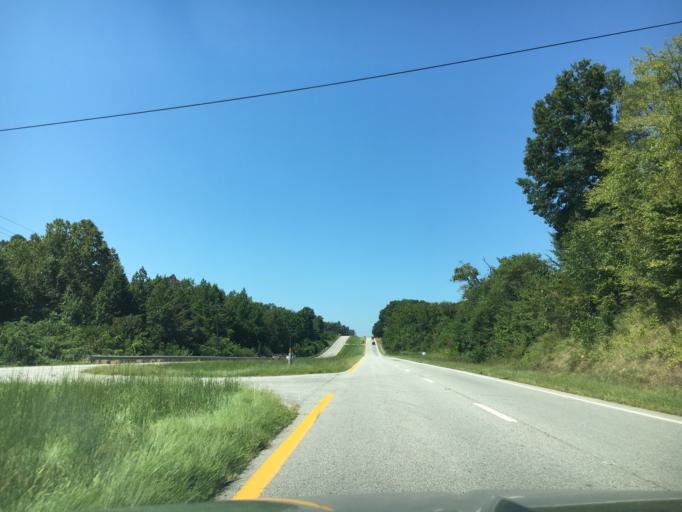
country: US
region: Virginia
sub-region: City of Danville
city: Danville
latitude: 36.5809
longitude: -79.2909
